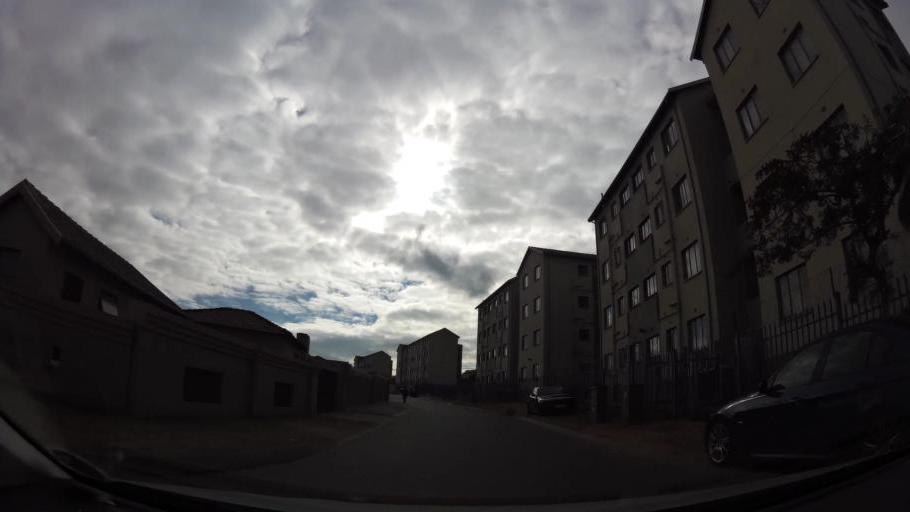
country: ZA
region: Gauteng
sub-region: City of Johannesburg Metropolitan Municipality
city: Roodepoort
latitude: -26.1905
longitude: 27.9084
